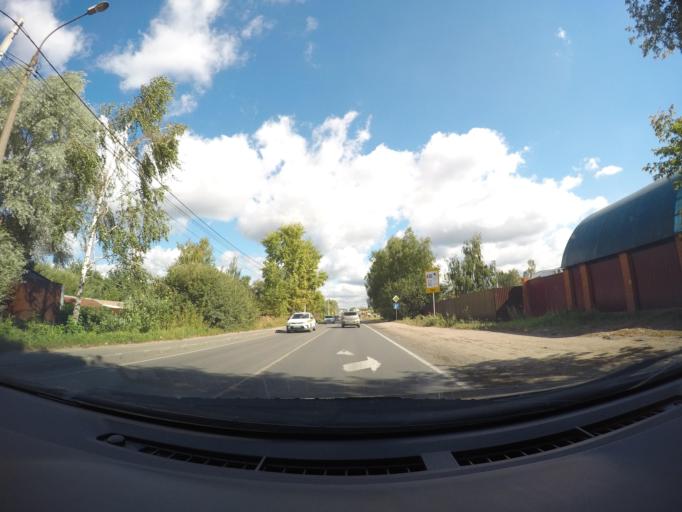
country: RU
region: Moskovskaya
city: Ramenskoye
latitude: 55.5849
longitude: 38.2472
